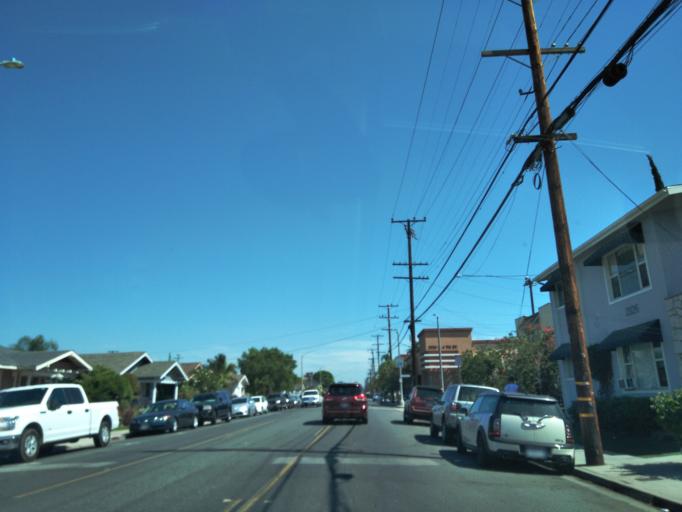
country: US
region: California
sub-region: Los Angeles County
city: Long Beach
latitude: 33.7717
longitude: -118.1585
